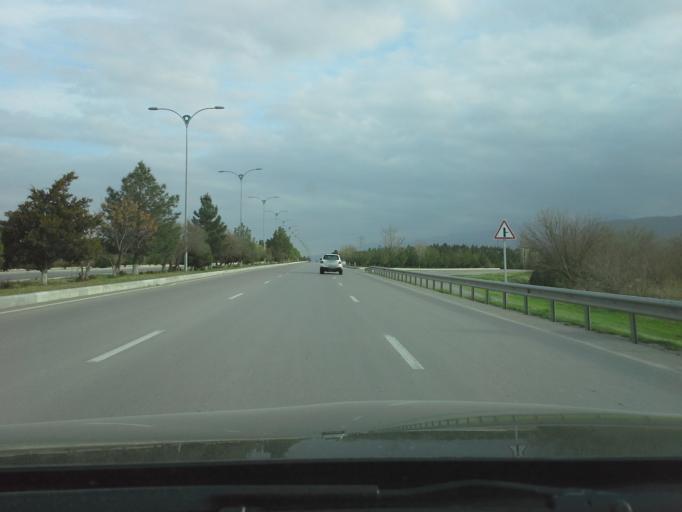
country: TM
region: Ahal
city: Abadan
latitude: 37.9536
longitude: 58.2274
